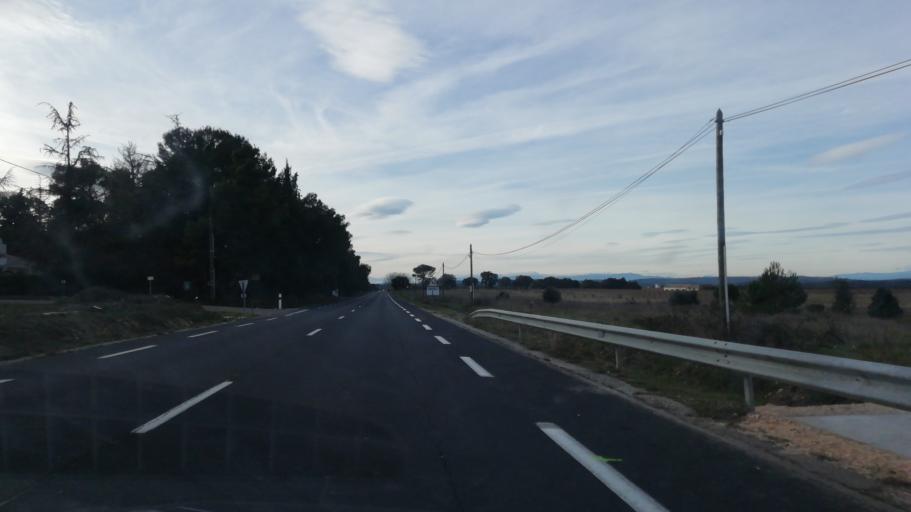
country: FR
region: Languedoc-Roussillon
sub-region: Departement du Gard
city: Caveirac
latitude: 43.8562
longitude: 4.2457
